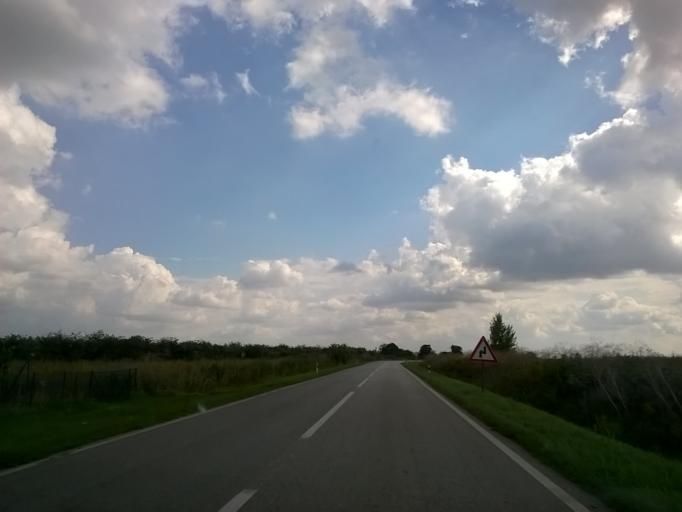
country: RS
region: Autonomna Pokrajina Vojvodina
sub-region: Juznobanatski Okrug
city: Vrsac
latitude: 45.1362
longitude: 21.2699
